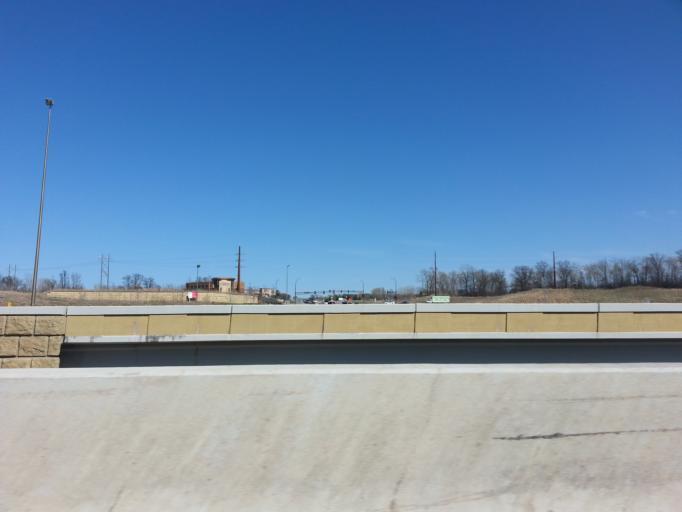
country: US
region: Minnesota
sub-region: Dakota County
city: Lakeville
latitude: 44.6816
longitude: -93.2935
